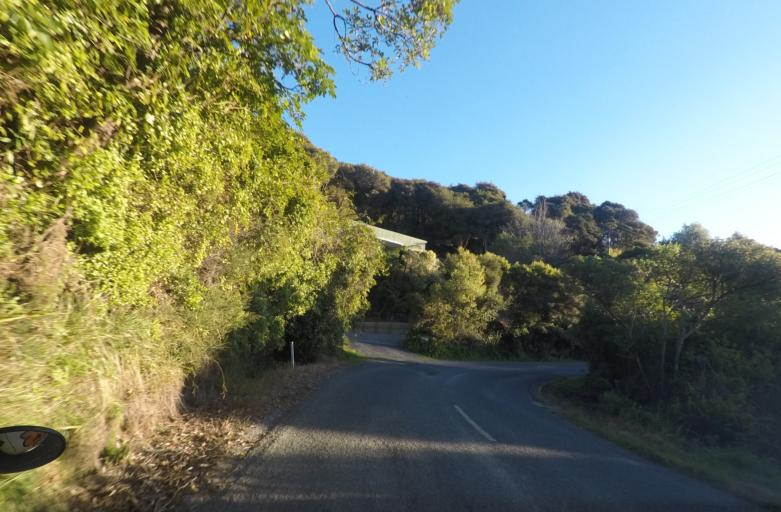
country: NZ
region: Marlborough
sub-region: Marlborough District
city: Picton
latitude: -41.2736
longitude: 173.9608
